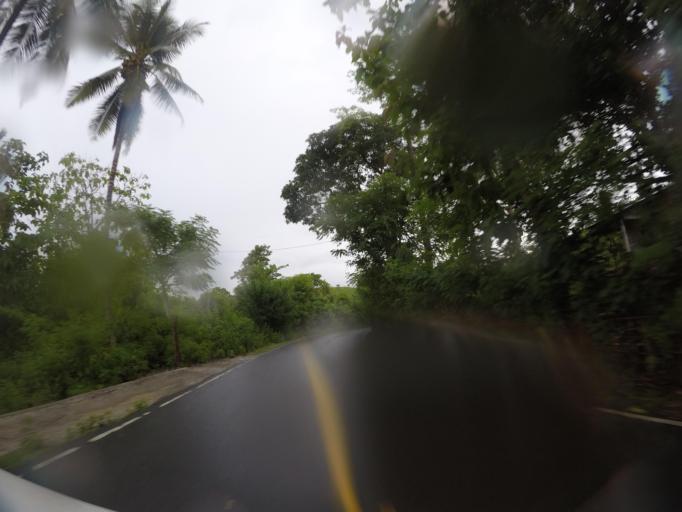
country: TL
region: Bobonaro
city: Maliana
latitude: -8.9692
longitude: 125.0470
